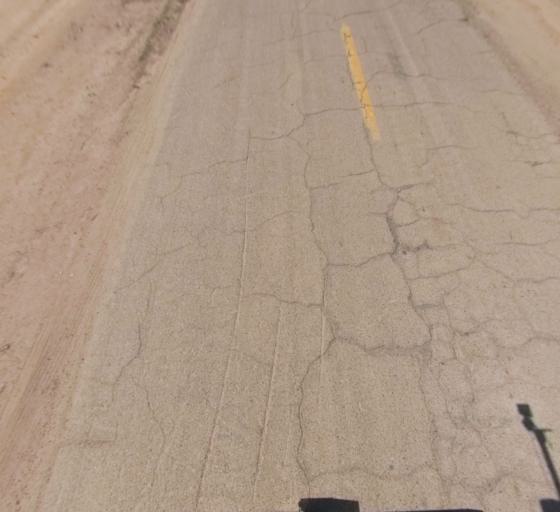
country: US
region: California
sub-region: Fresno County
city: Biola
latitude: 36.8531
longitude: -119.9293
